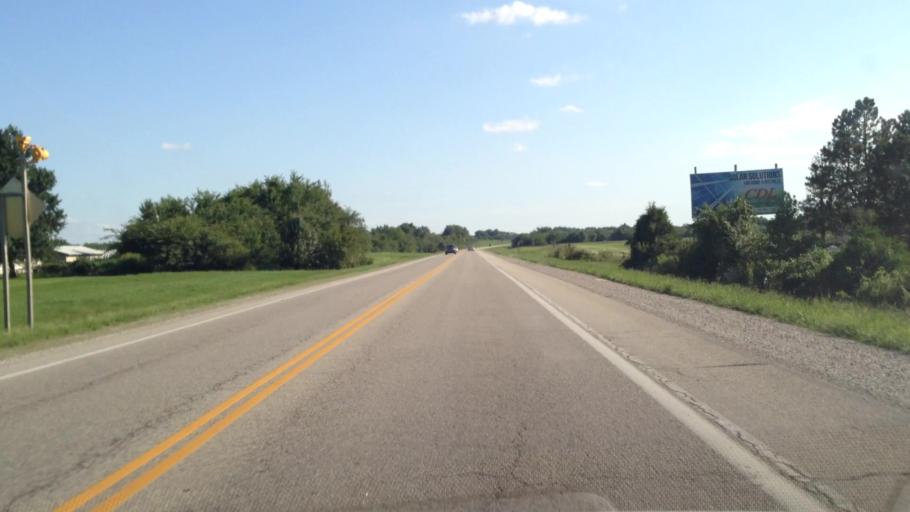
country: US
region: Kansas
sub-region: Crawford County
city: Arma
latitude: 37.5408
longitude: -94.7102
